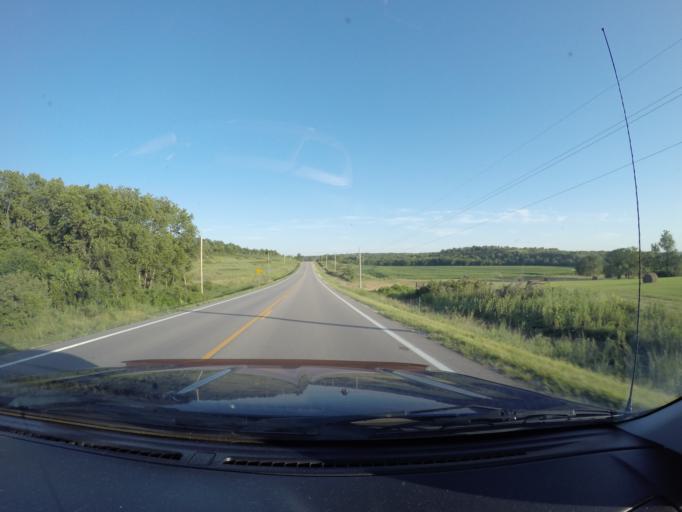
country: US
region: Kansas
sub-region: Pottawatomie County
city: Wamego
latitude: 39.1342
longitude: -96.3015
